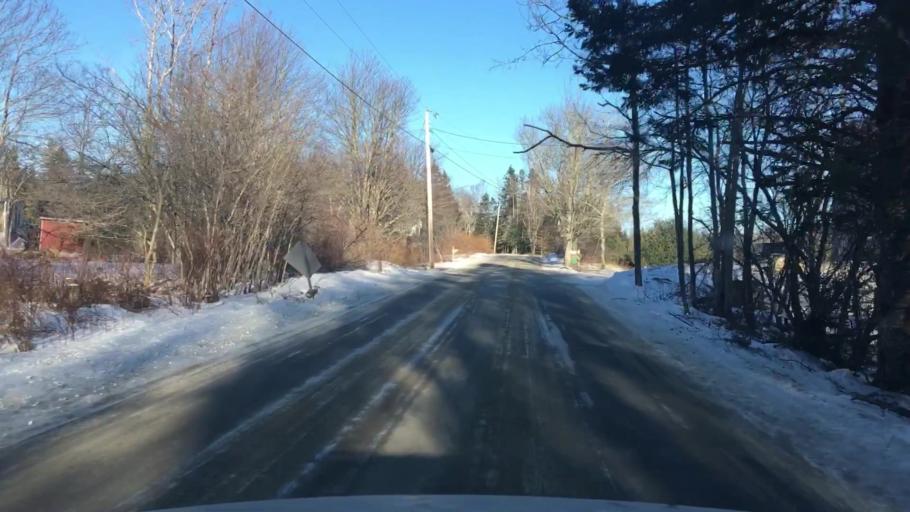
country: US
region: Maine
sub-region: Hancock County
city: Penobscot
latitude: 44.3864
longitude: -68.7195
